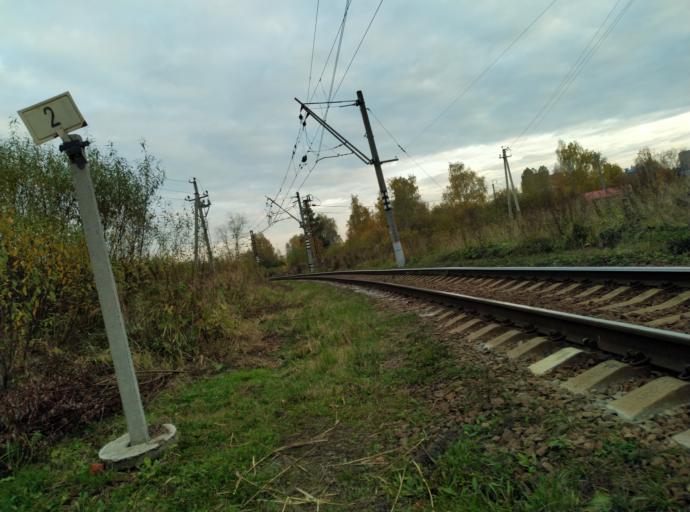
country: RU
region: Moskovskaya
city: Bol'shiye Vyazemy
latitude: 55.6161
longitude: 36.9729
